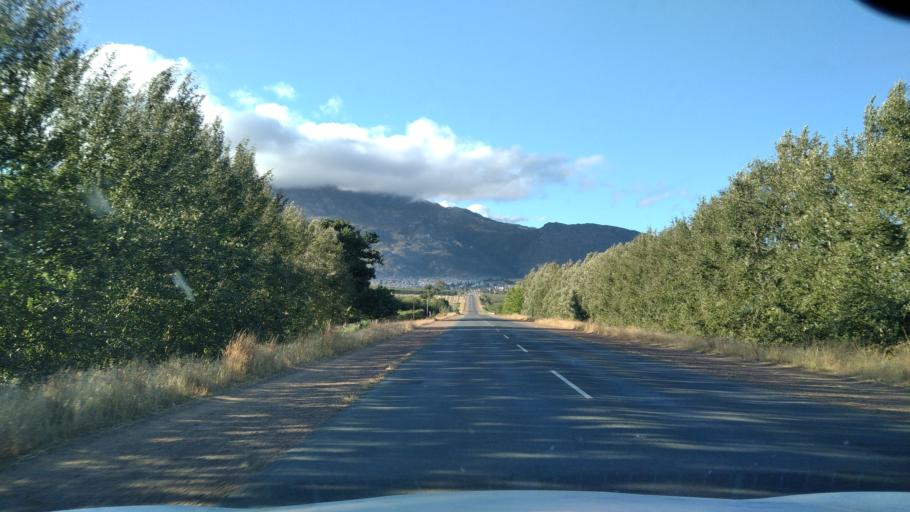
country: ZA
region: Western Cape
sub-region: Overberg District Municipality
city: Caledon
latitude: -34.0085
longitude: 19.2930
